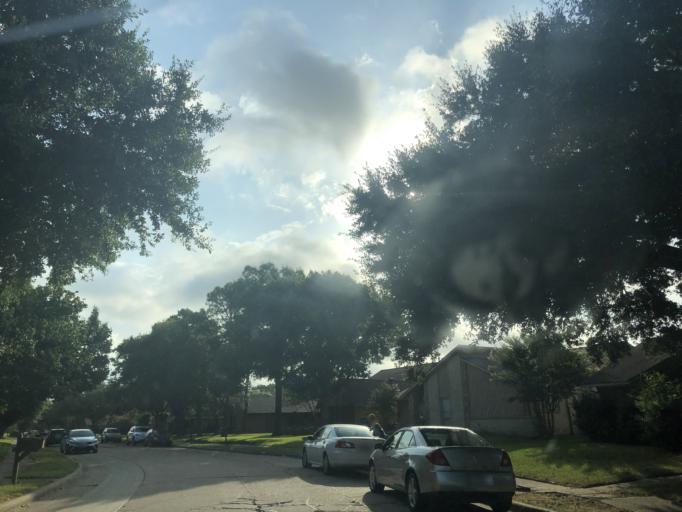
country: US
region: Texas
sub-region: Dallas County
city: Garland
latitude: 32.8501
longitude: -96.6282
